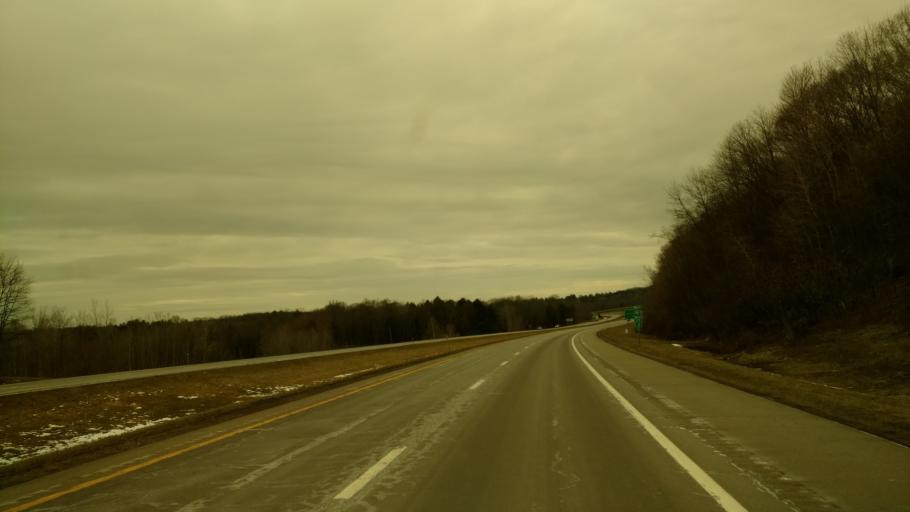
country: US
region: New York
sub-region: Chautauqua County
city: Falconer
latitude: 42.1246
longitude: -79.2154
